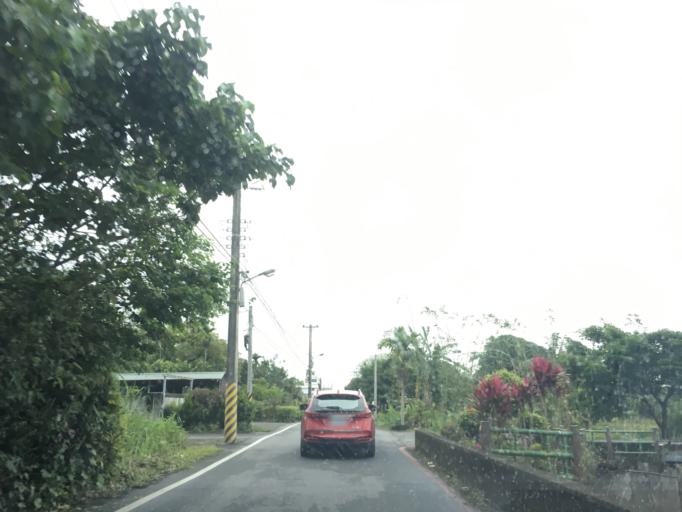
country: TW
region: Taiwan
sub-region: Hualien
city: Hualian
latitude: 23.9878
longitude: 121.5693
